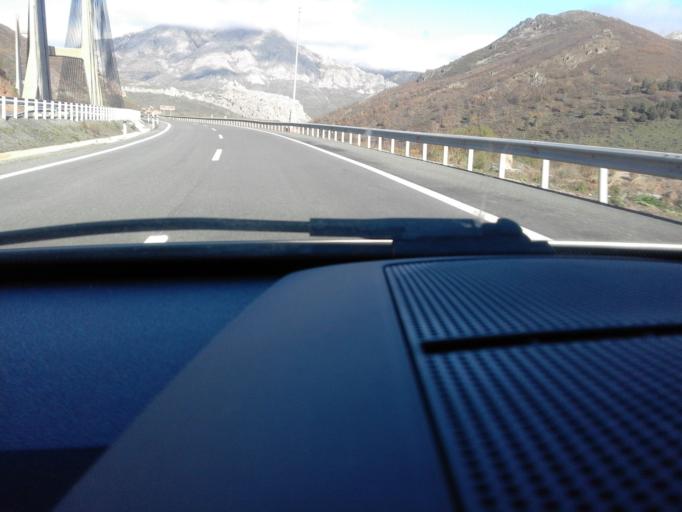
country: ES
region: Castille and Leon
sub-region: Provincia de Leon
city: Sena de Luna
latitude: 42.8914
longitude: -5.8866
